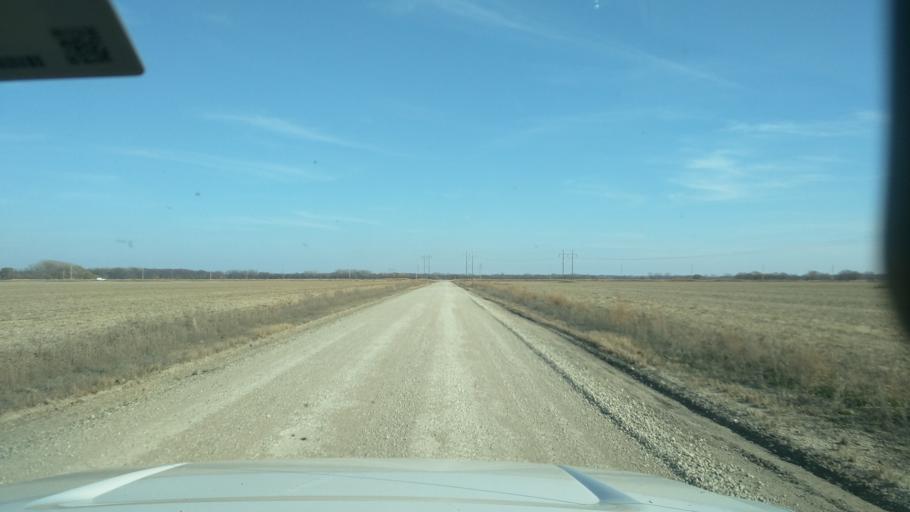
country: US
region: Kansas
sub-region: Lyon County
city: Emporia
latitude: 38.3760
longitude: -96.1873
